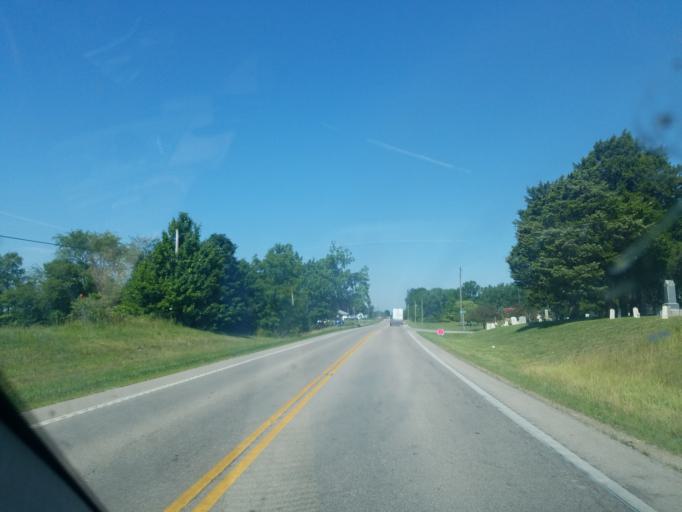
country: US
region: Ohio
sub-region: Shelby County
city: Jackson Center
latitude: 40.4394
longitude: -84.0202
